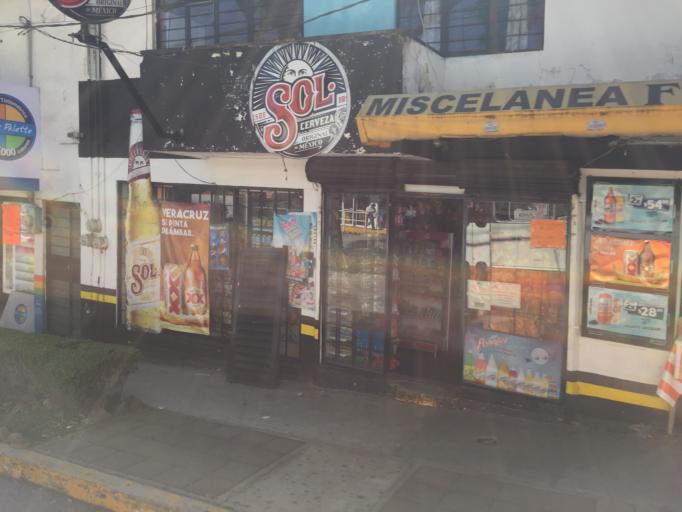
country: MX
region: Veracruz
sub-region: Xalapa
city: Xalapa de Enriquez
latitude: 19.5360
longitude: -96.9126
